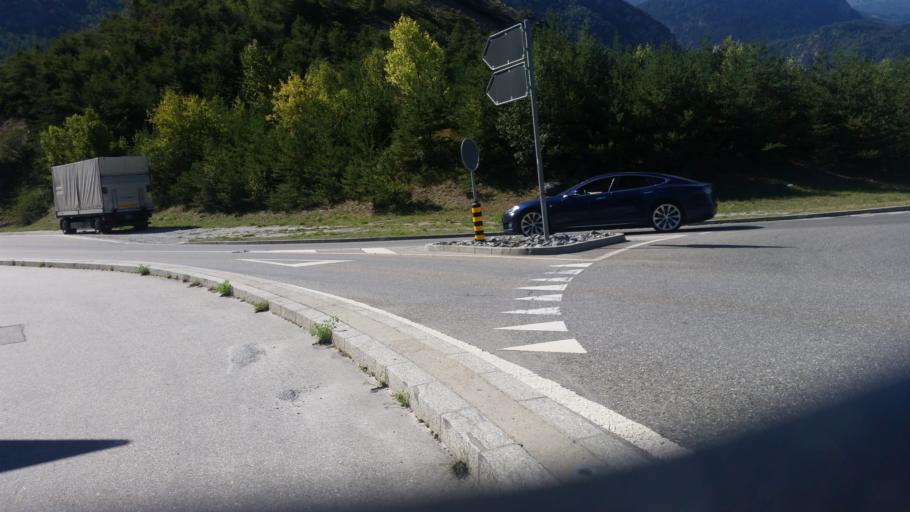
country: CH
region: Valais
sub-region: Sierre District
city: Chippis
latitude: 46.2933
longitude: 7.5578
